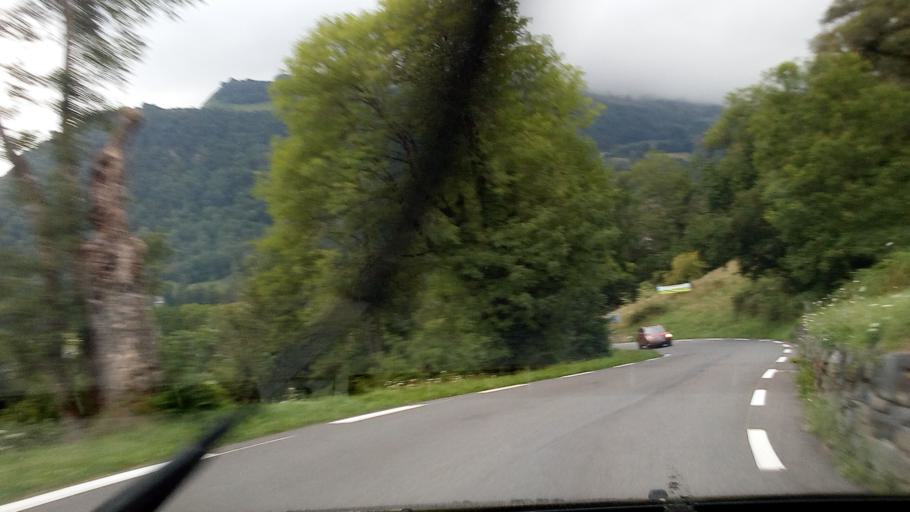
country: FR
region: Midi-Pyrenees
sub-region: Departement des Hautes-Pyrenees
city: Cauterets
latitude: 42.9585
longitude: -0.2137
